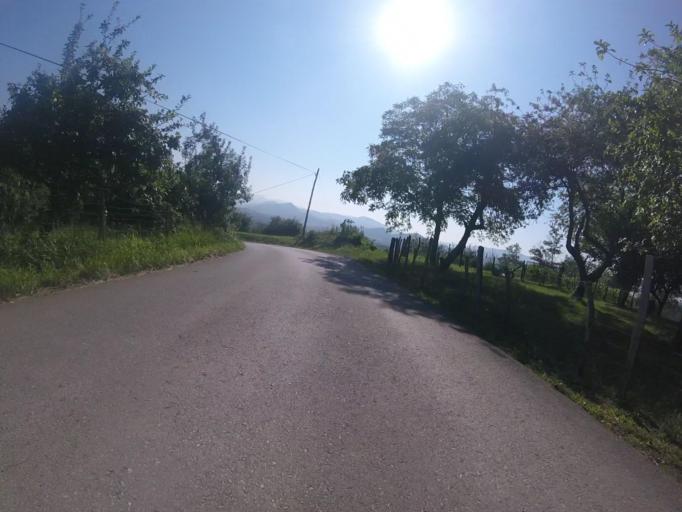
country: ES
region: Basque Country
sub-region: Provincia de Guipuzcoa
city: Astigarraga
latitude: 43.2650
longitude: -1.9357
